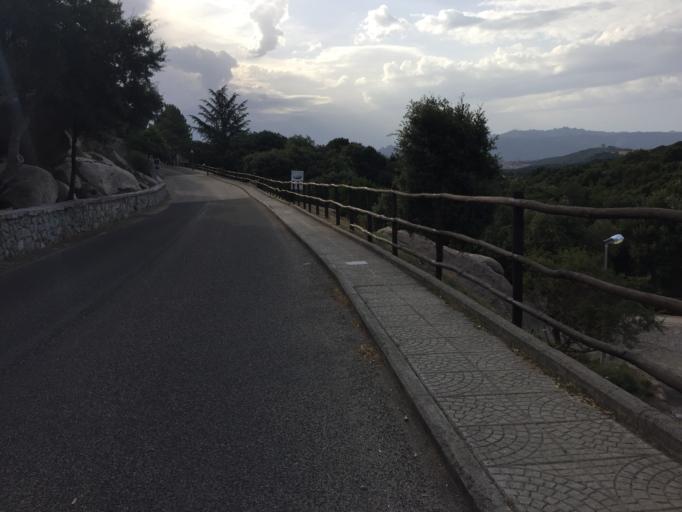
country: IT
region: Sardinia
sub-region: Provincia di Olbia-Tempio
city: Aggius
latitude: 40.9283
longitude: 9.0587
